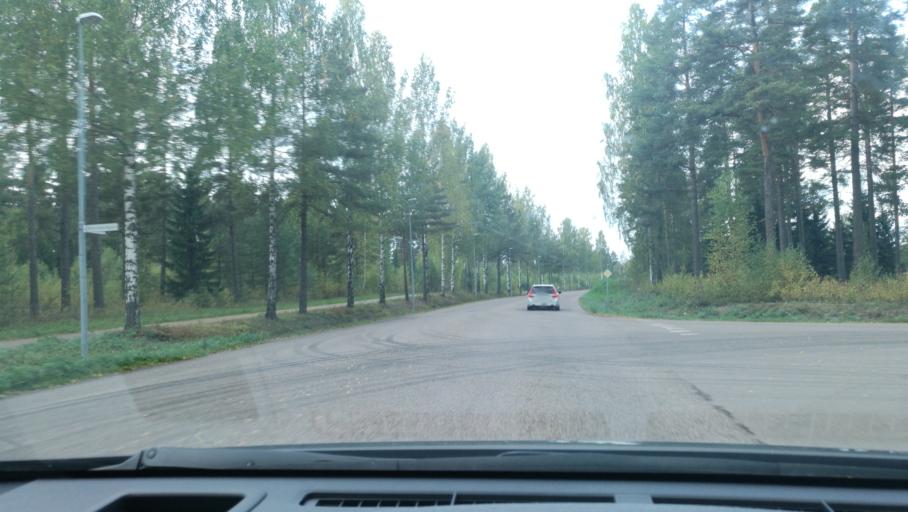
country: SE
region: Dalarna
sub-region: Avesta Kommun
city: Avesta
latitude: 60.1571
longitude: 16.1977
